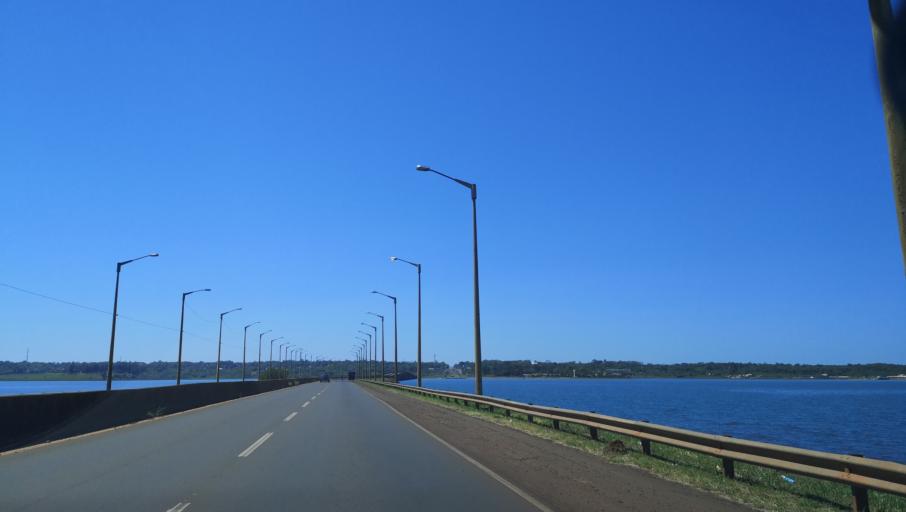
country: PY
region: Itapua
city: Encarnacion
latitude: -27.2953
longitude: -55.9088
